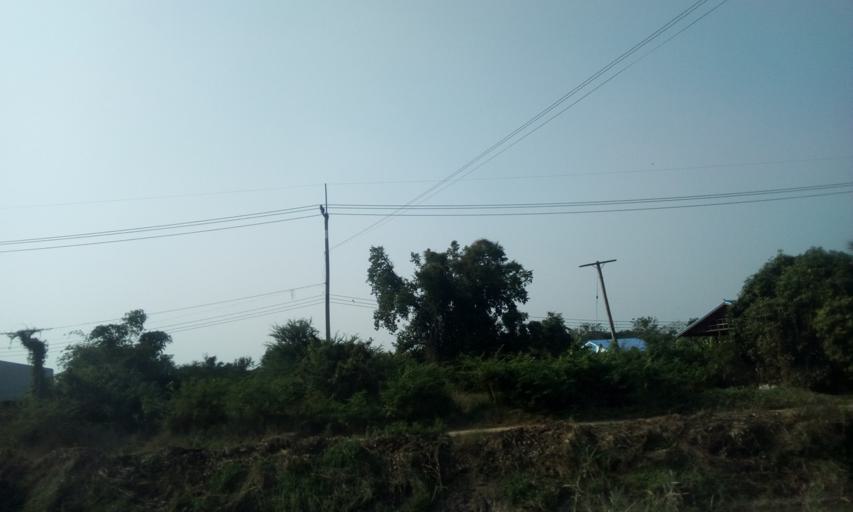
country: TH
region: Sing Buri
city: Tha Chang
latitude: 14.7331
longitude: 100.4325
